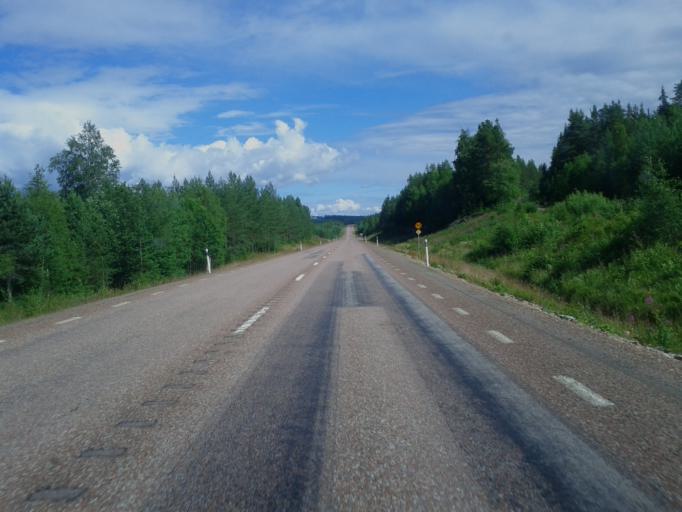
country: SE
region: Dalarna
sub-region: Rattviks Kommun
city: Raettvik
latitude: 60.8435
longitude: 15.1887
